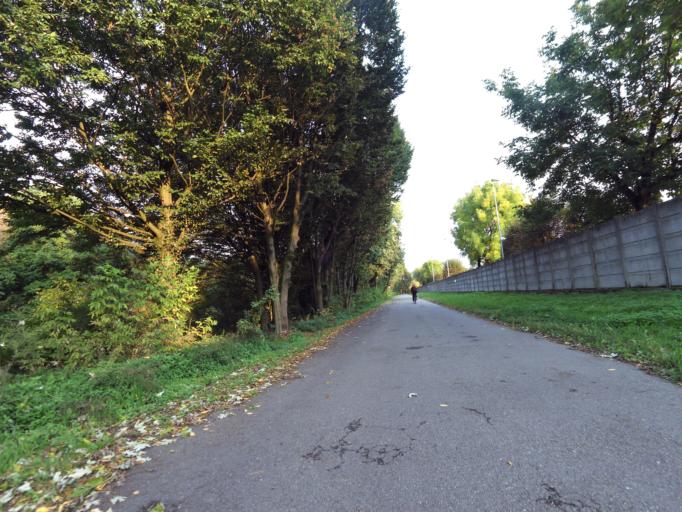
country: IT
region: Lombardy
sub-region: Citta metropolitana di Milano
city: San Donato Milanese
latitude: 45.4198
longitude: 9.2858
